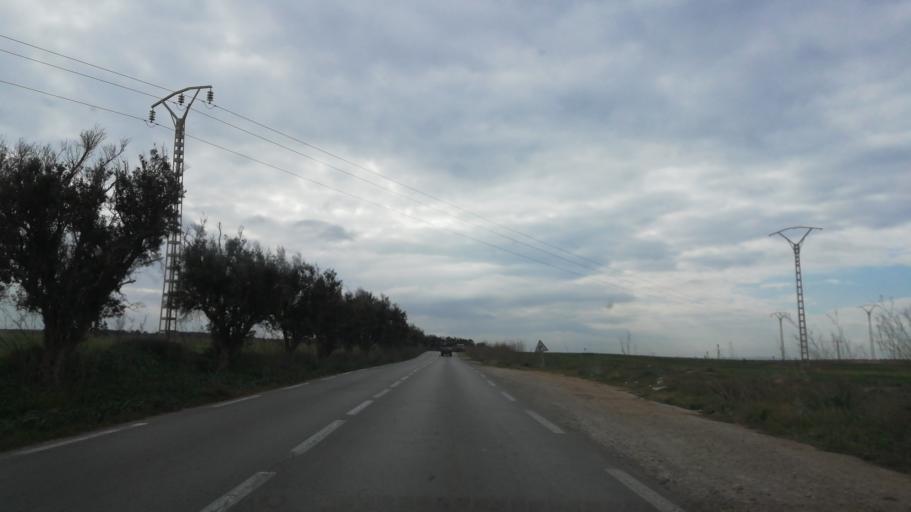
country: DZ
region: Oran
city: Ain el Bya
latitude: 35.7555
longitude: -0.3508
